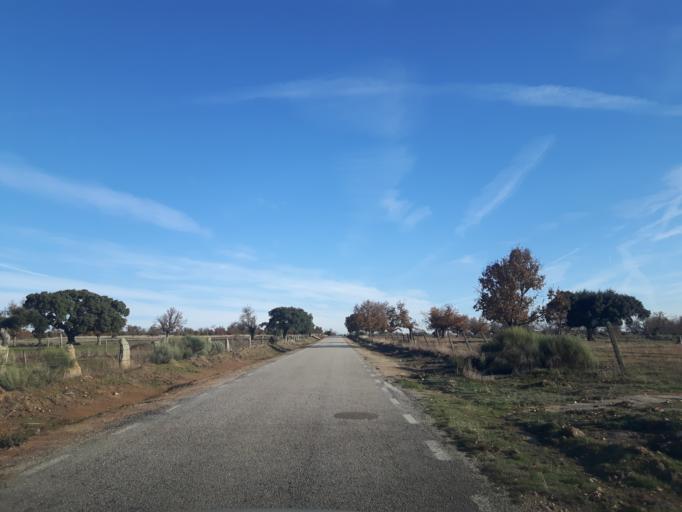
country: ES
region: Castille and Leon
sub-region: Provincia de Salamanca
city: Cerralbo
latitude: 40.9498
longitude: -6.6064
